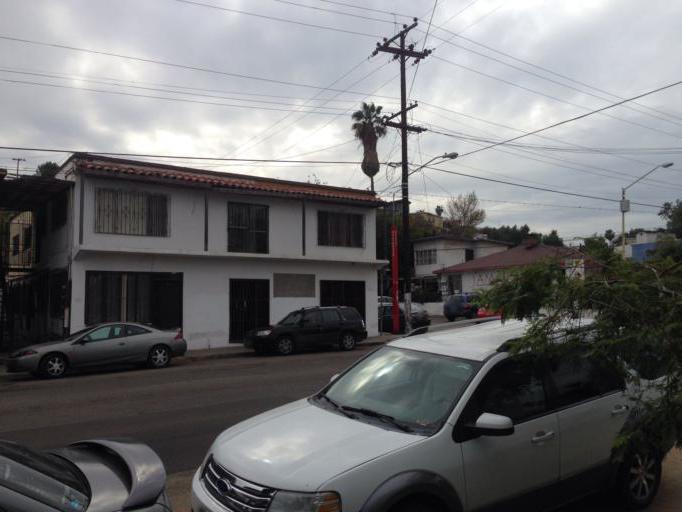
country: MX
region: Baja California
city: Tijuana
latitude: 32.5301
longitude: -117.0445
